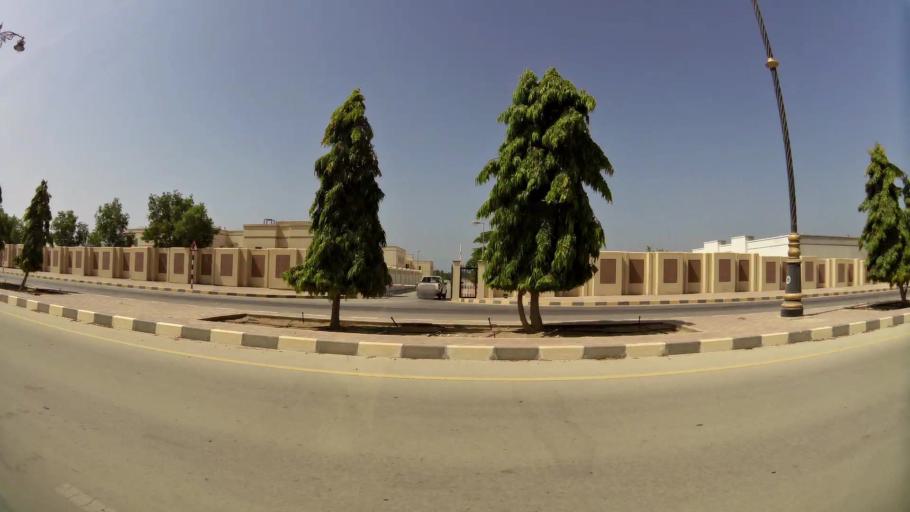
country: OM
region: Zufar
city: Salalah
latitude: 17.0263
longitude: 54.1511
